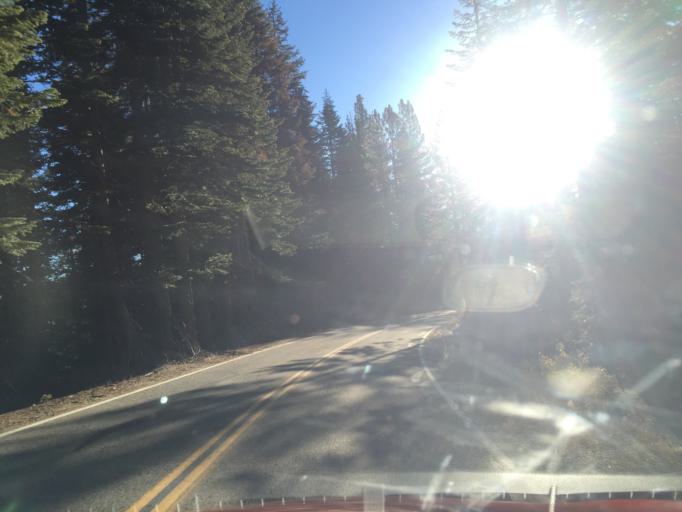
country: US
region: California
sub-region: Mariposa County
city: Yosemite Valley
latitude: 37.6739
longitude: -119.6381
